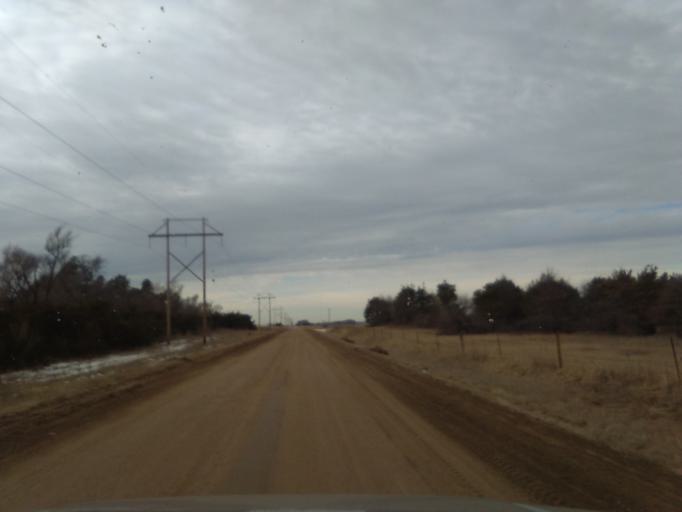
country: US
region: Nebraska
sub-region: Buffalo County
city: Gibbon
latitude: 40.6550
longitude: -98.7784
